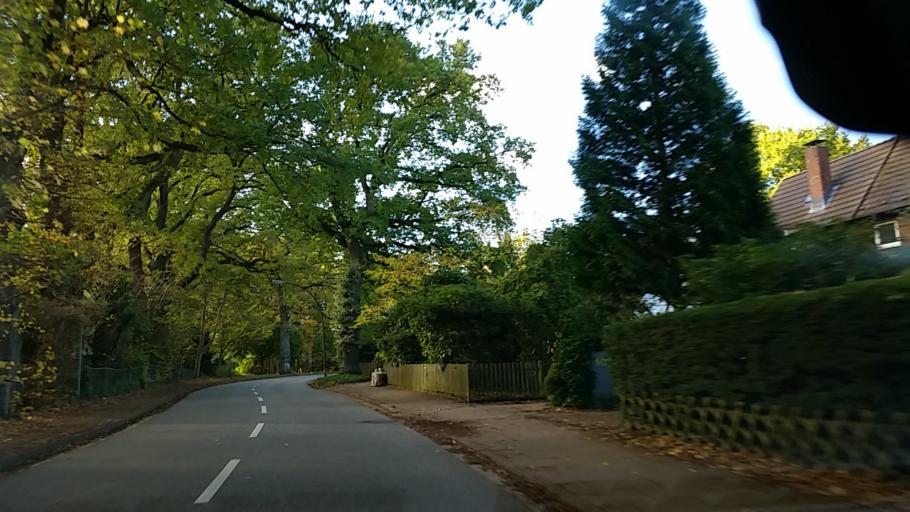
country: DE
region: Schleswig-Holstein
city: Halstenbek
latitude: 53.5698
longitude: 9.8370
